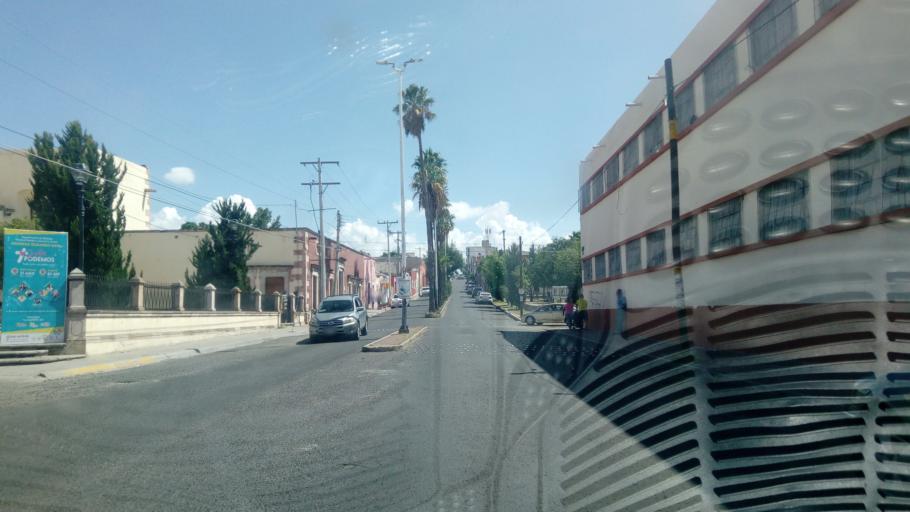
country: MX
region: Durango
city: Victoria de Durango
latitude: 24.0192
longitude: -104.6727
